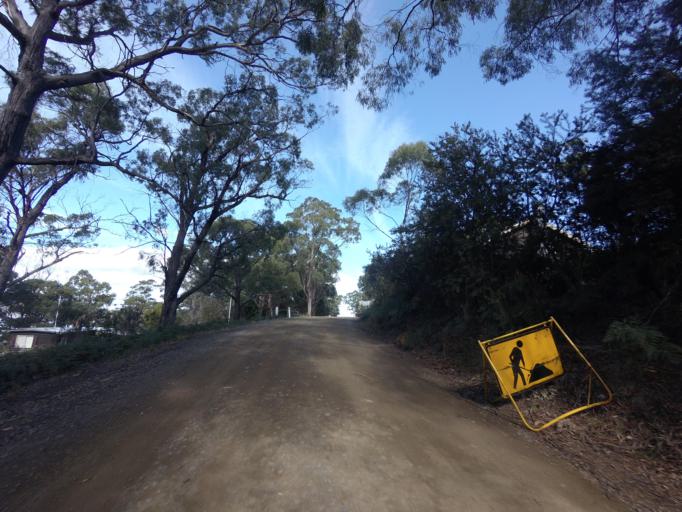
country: AU
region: Tasmania
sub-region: Clarence
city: Sandford
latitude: -42.9916
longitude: 147.7130
